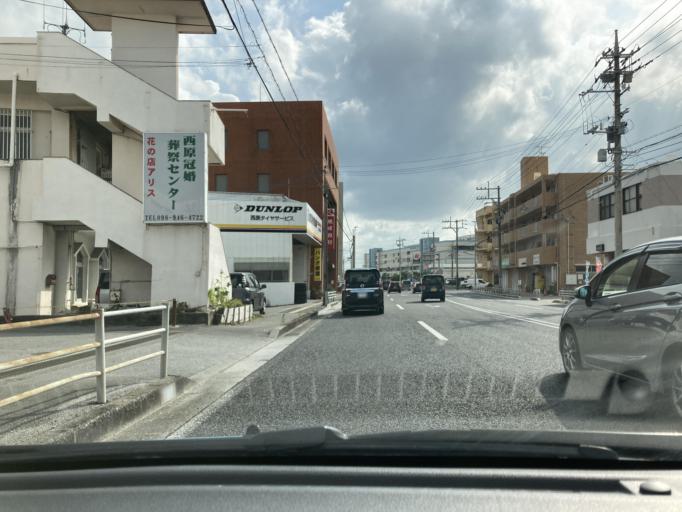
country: JP
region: Okinawa
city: Ginowan
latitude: 26.2269
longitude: 127.7668
